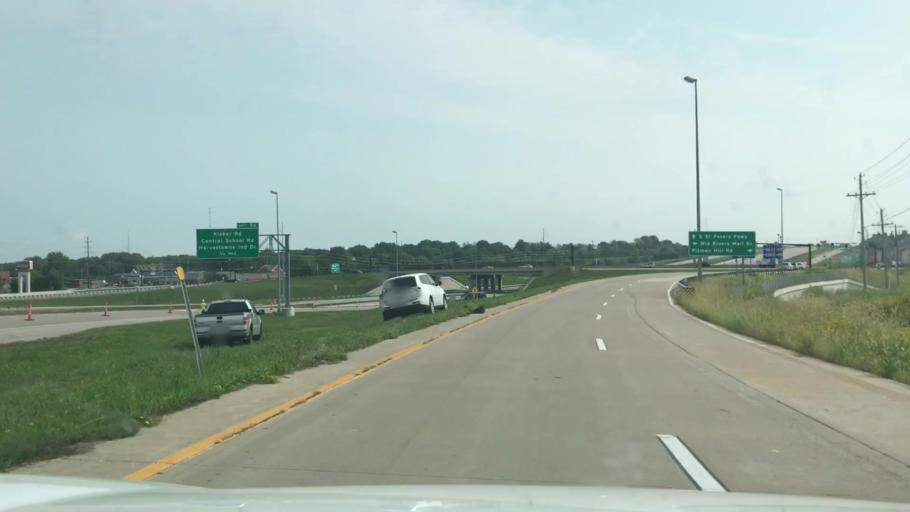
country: US
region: Missouri
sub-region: Saint Charles County
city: Cottleville
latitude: 38.7361
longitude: -90.6359
